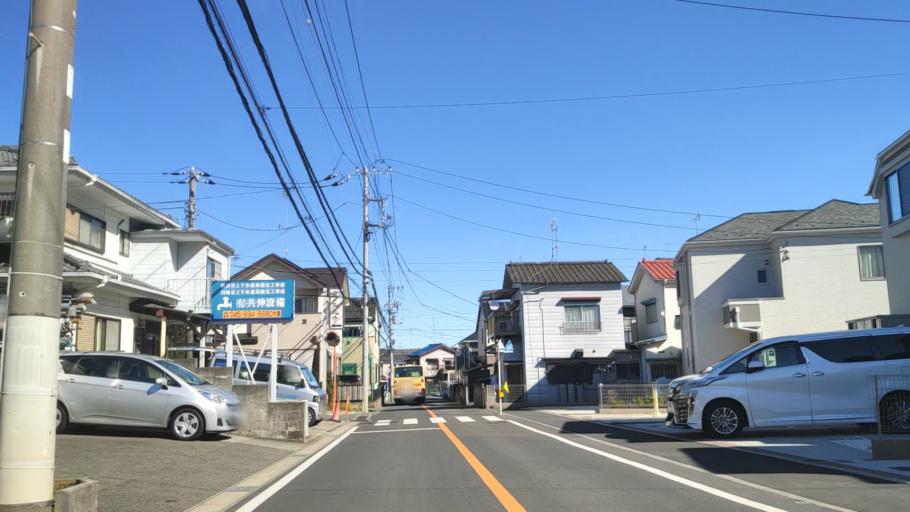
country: JP
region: Tokyo
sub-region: Machida-shi
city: Machida
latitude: 35.5130
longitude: 139.5279
